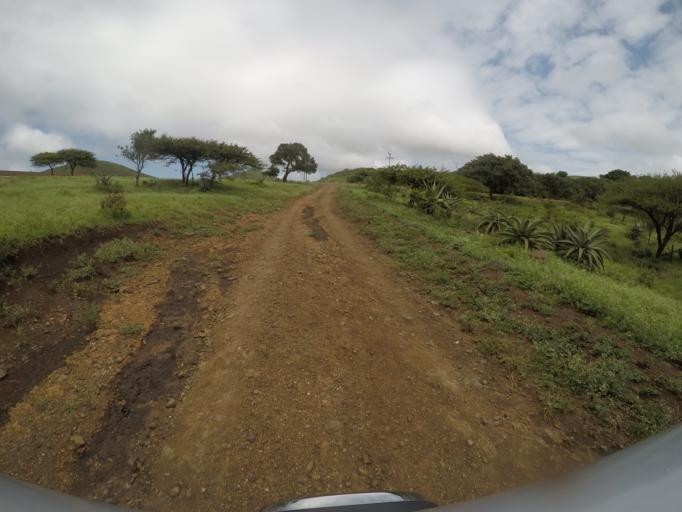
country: ZA
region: KwaZulu-Natal
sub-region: uThungulu District Municipality
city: Empangeni
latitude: -28.6272
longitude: 31.8716
